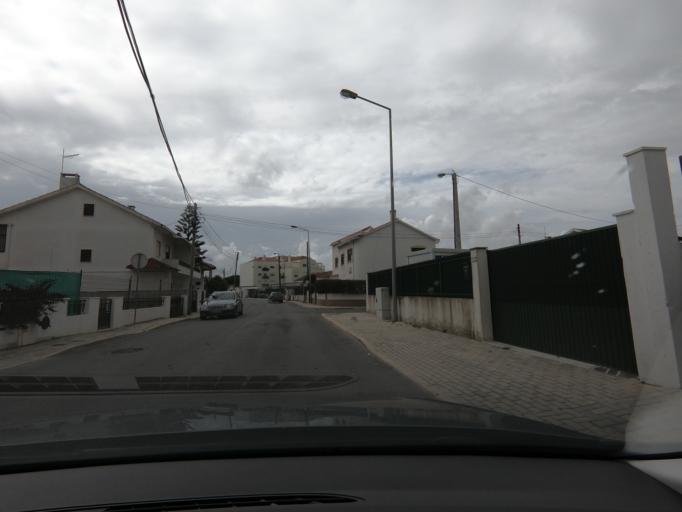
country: PT
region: Lisbon
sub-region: Cascais
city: Sao Domingos de Rana
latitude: 38.7364
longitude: -9.3364
